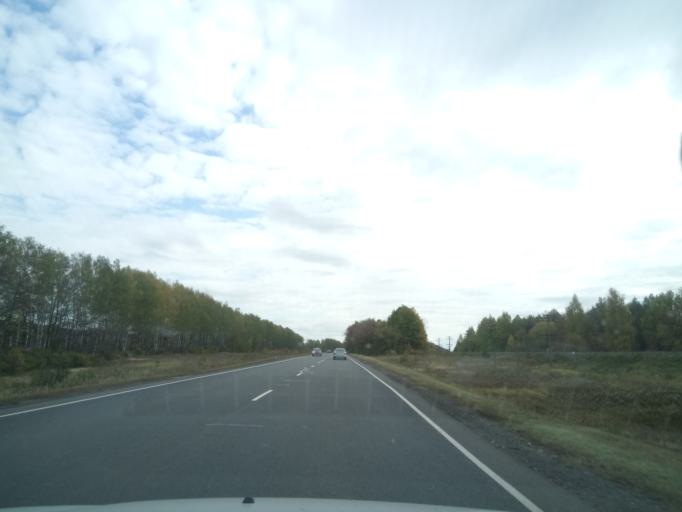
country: RU
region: Nizjnij Novgorod
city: Lukoyanov
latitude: 55.0643
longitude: 44.3520
